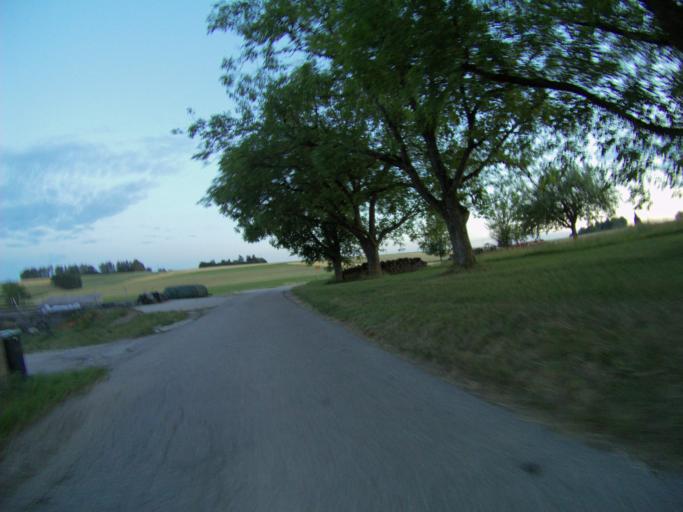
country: DE
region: Bavaria
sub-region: Upper Bavaria
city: Marzling
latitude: 48.4277
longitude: 11.7813
